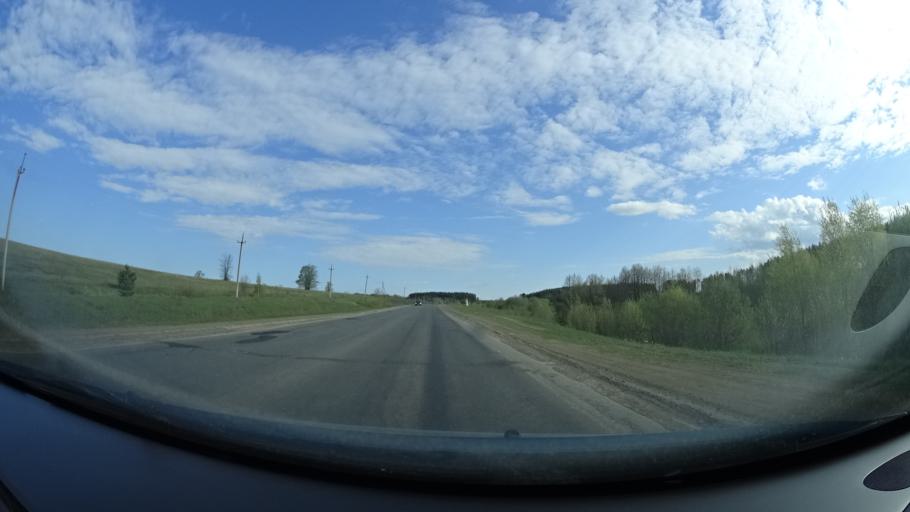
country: RU
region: Bashkortostan
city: Blagoveshchensk
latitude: 55.0789
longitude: 55.8073
